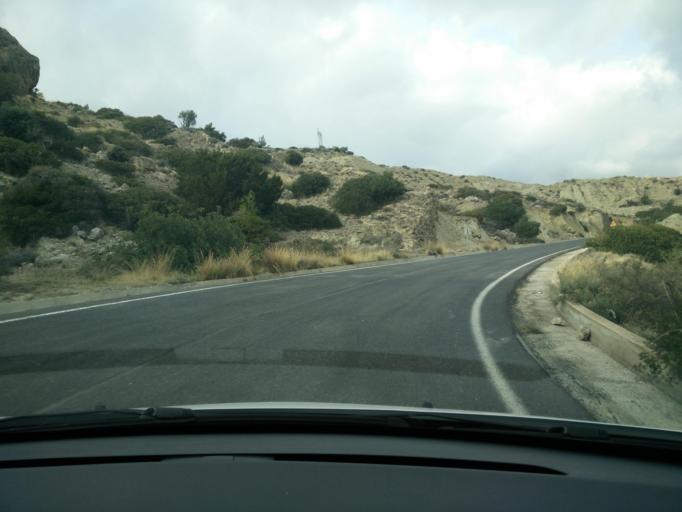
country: GR
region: Crete
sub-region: Nomos Lasithiou
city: Gra Liyia
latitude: 35.0173
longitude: 25.5788
